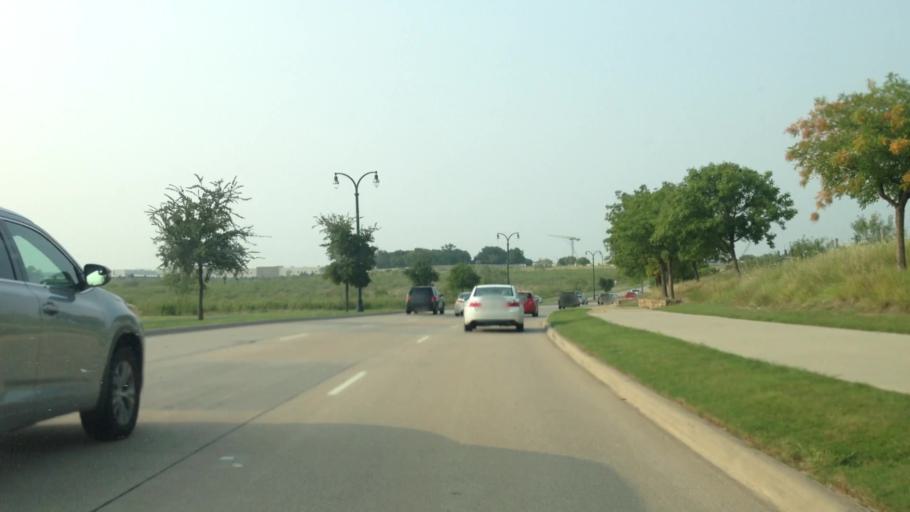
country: US
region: Texas
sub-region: Denton County
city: The Colony
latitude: 33.0612
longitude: -96.8626
